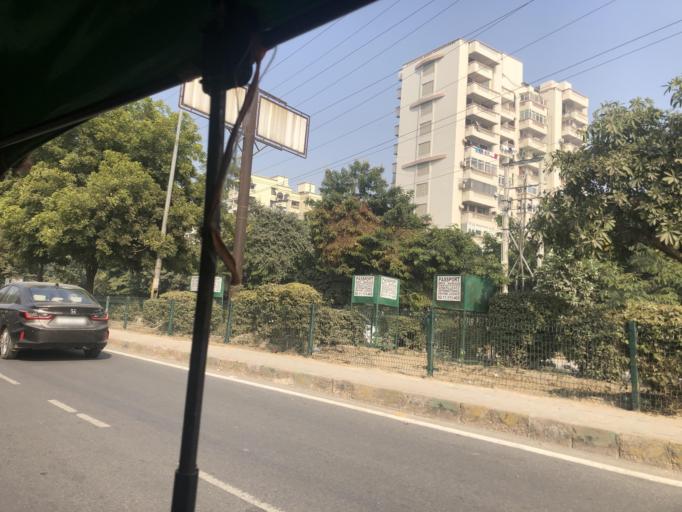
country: IN
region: Haryana
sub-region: Gurgaon
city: Gurgaon
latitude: 28.4477
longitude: 77.0790
